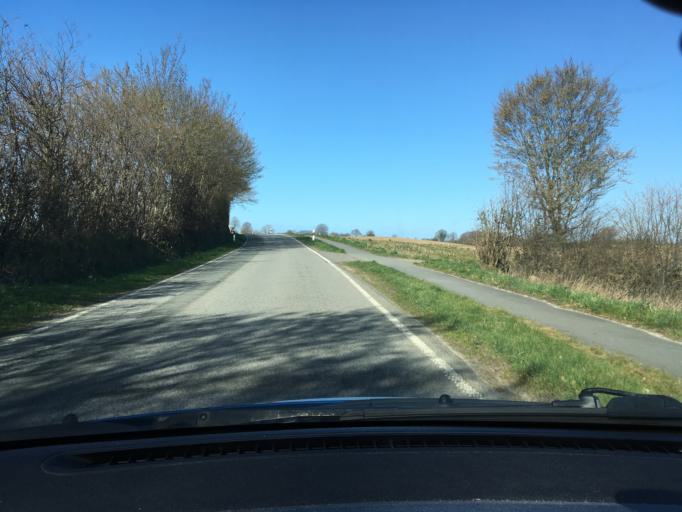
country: DE
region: Schleswig-Holstein
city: Fahrdorf
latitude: 54.5041
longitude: 9.6282
